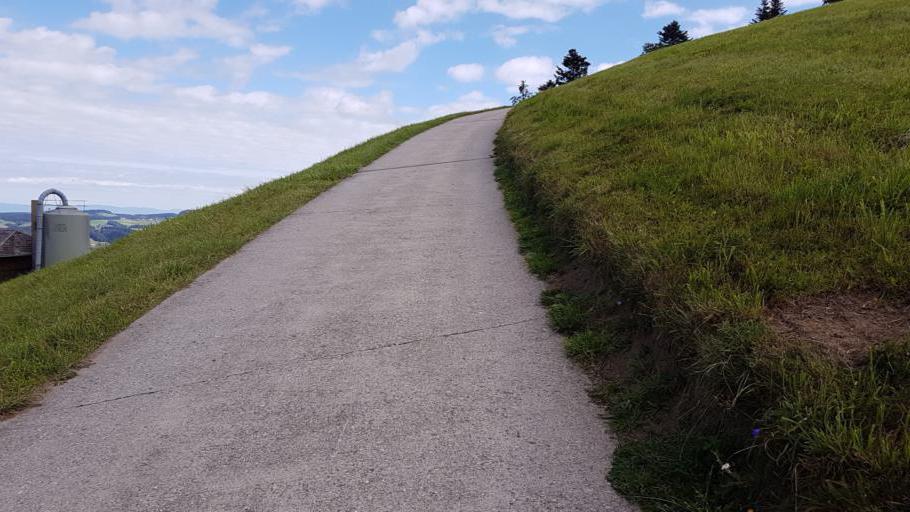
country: CH
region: Bern
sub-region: Bern-Mittelland District
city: Linden
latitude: 46.8603
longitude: 7.6823
